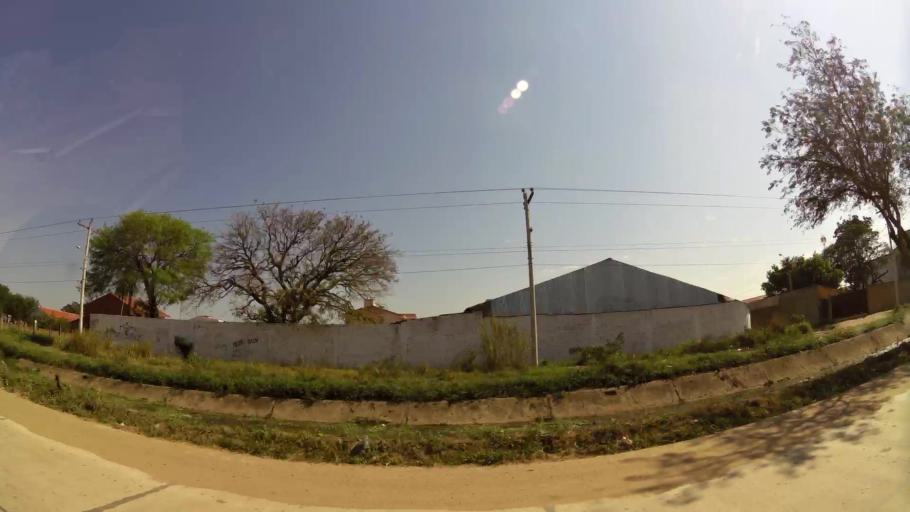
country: BO
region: Santa Cruz
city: Cotoca
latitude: -17.7583
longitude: -63.0917
